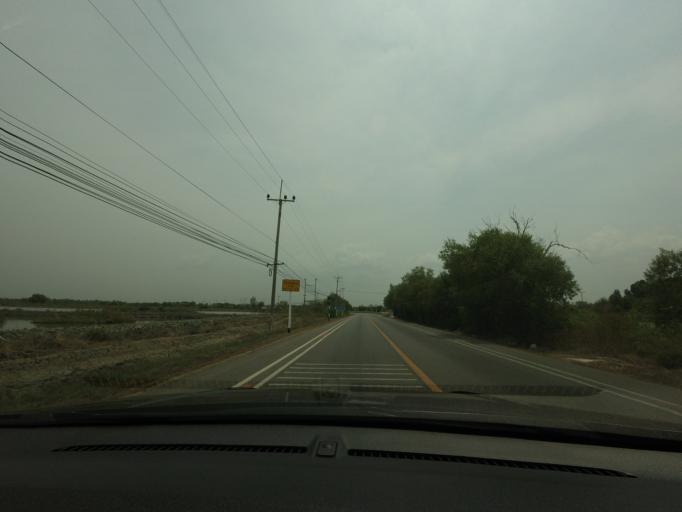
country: TH
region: Ratchaburi
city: Pak Tho
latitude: 13.3161
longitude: 99.9163
